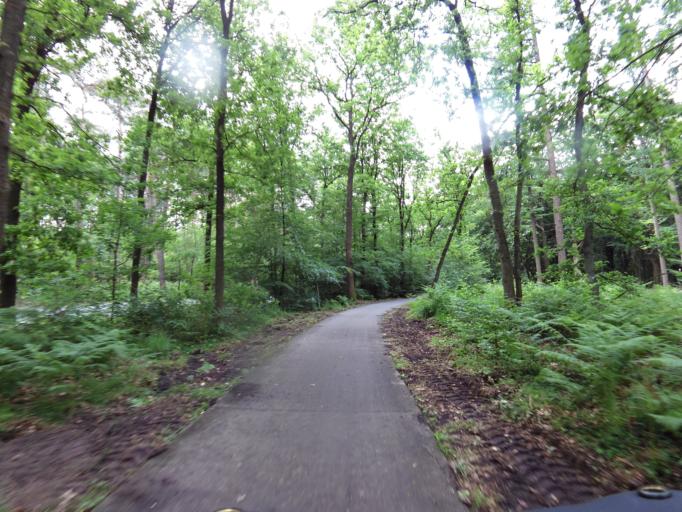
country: NL
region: Gelderland
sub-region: Gemeente Apeldoorn
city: Uddel
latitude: 52.3013
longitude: 5.8061
